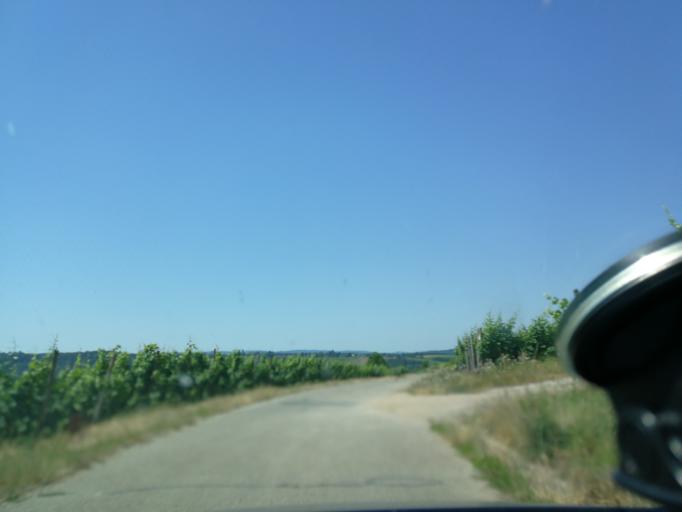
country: DE
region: Rheinland-Pfalz
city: Wintrich
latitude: 49.8779
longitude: 6.9397
